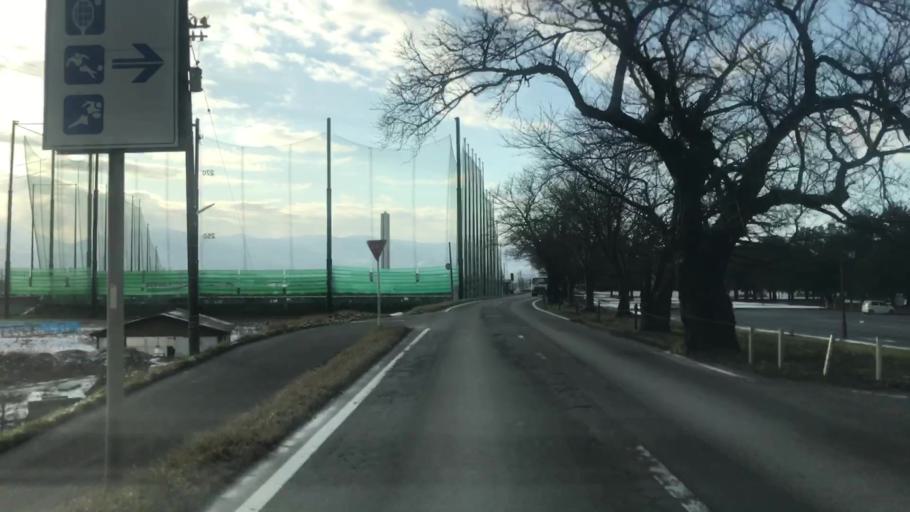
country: JP
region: Toyama
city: Toyama-shi
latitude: 36.6967
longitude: 137.2824
